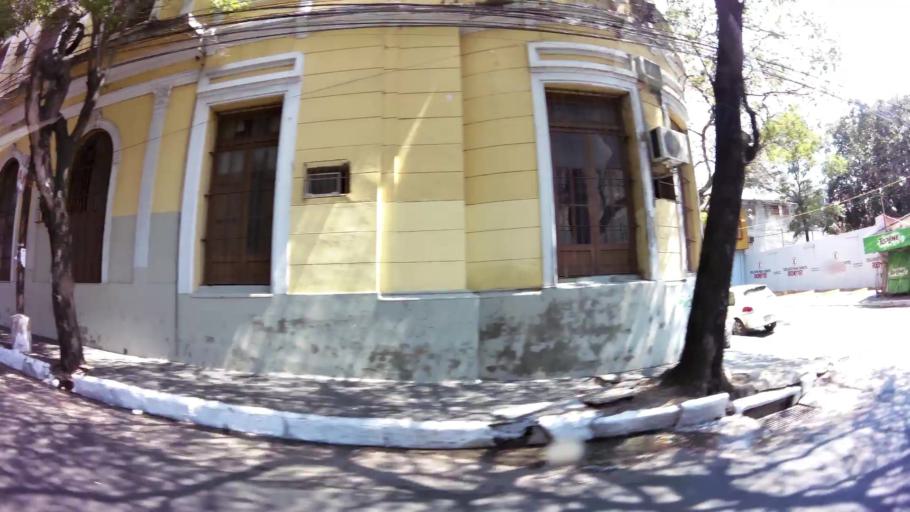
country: PY
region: Asuncion
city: Asuncion
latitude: -25.2842
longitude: -57.6357
